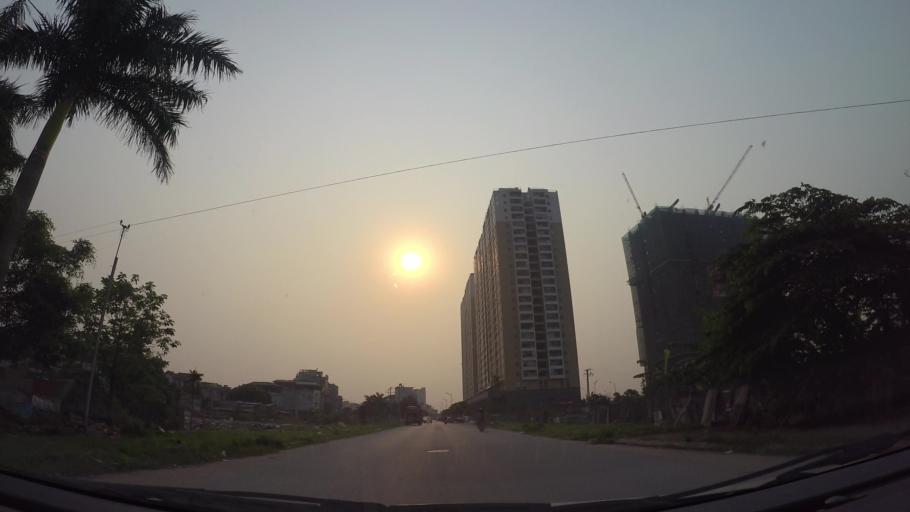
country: VN
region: Ha Noi
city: Cau Dien
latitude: 21.0086
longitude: 105.7236
